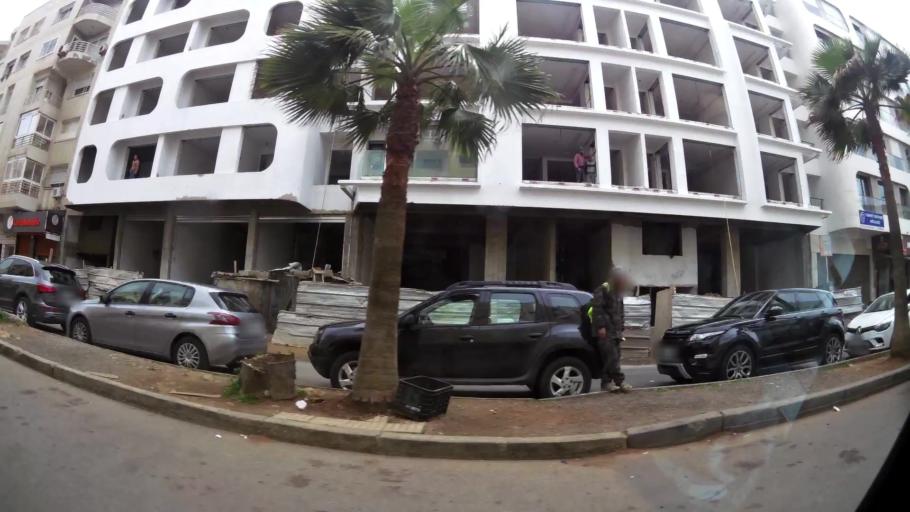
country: MA
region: Grand Casablanca
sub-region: Casablanca
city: Casablanca
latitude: 33.5997
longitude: -7.6483
